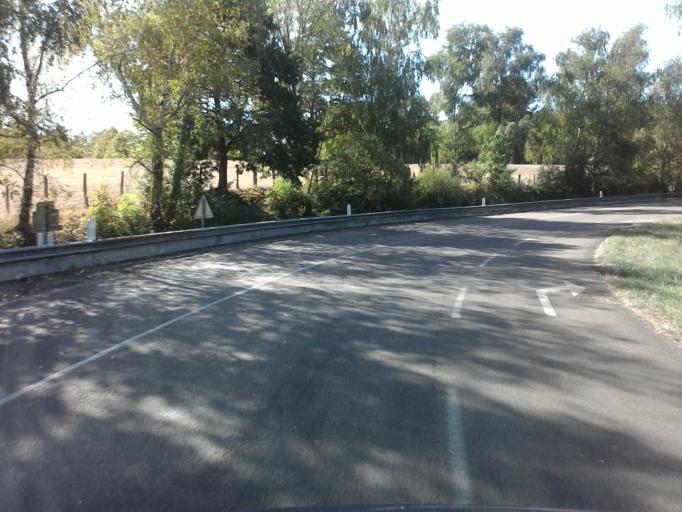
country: FR
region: Bourgogne
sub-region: Departement de la Cote-d'Or
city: Semur-en-Auxois
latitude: 47.4700
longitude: 4.3555
